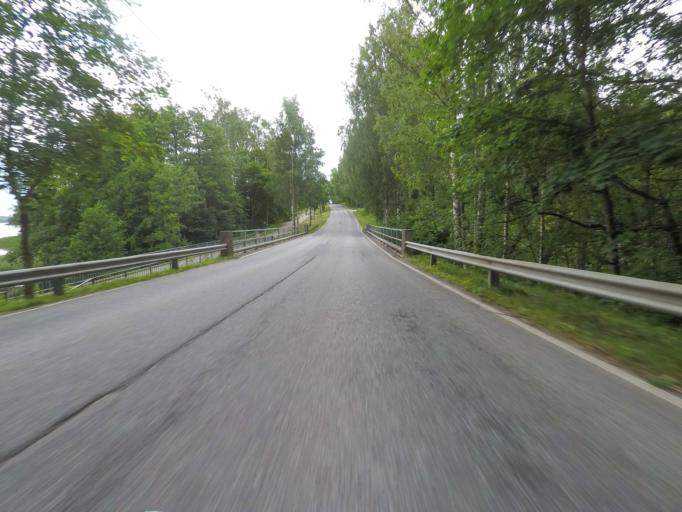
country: FI
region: Varsinais-Suomi
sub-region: Salo
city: Muurla
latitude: 60.3514
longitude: 23.2827
